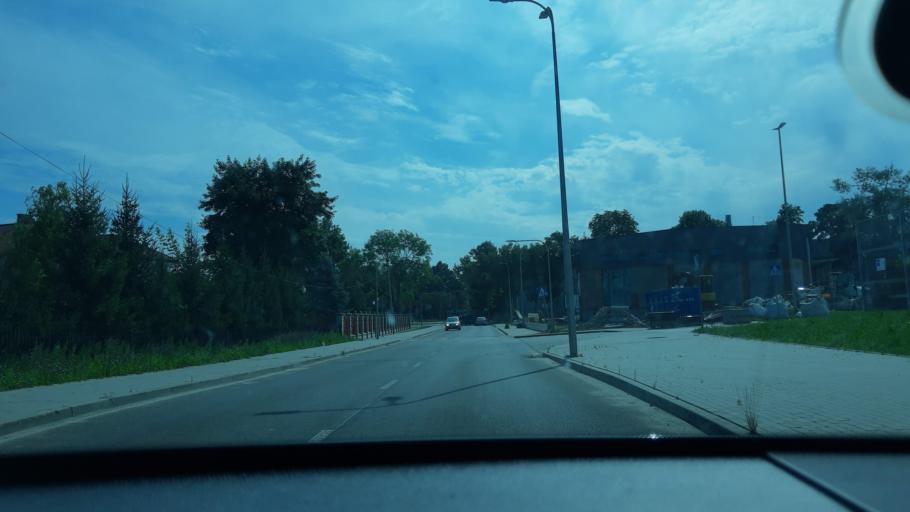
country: PL
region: Lodz Voivodeship
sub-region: Powiat sieradzki
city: Sieradz
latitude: 51.5982
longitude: 18.7320
